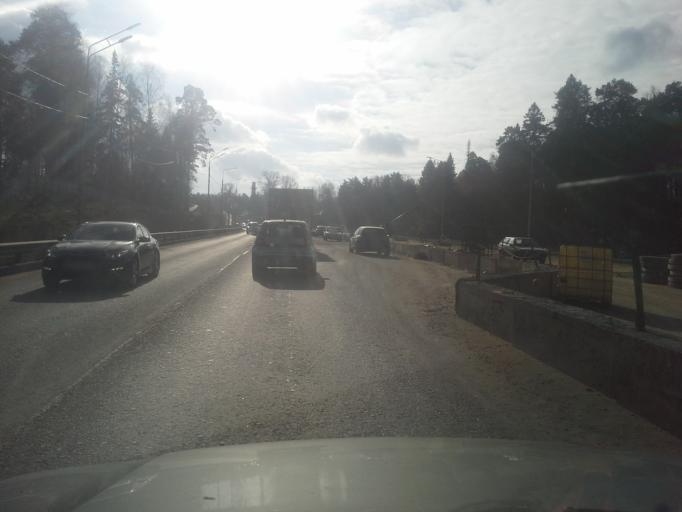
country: RU
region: Moskovskaya
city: Zvenigorod
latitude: 55.7100
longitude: 36.8740
